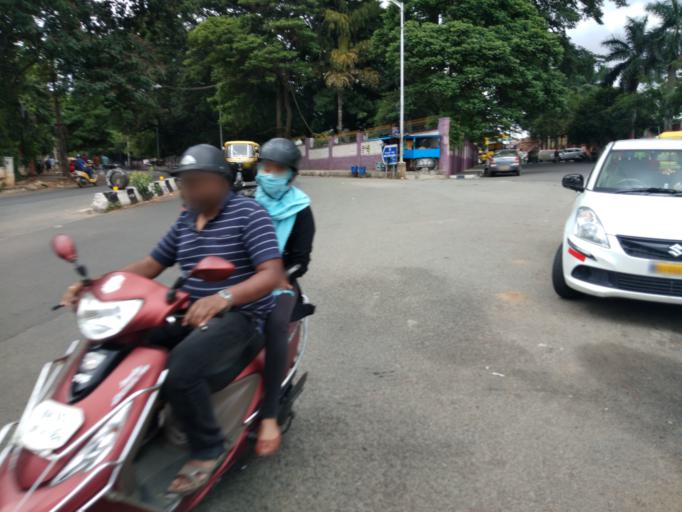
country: IN
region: Karnataka
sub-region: Bangalore Urban
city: Bangalore
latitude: 12.9947
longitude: 77.5969
